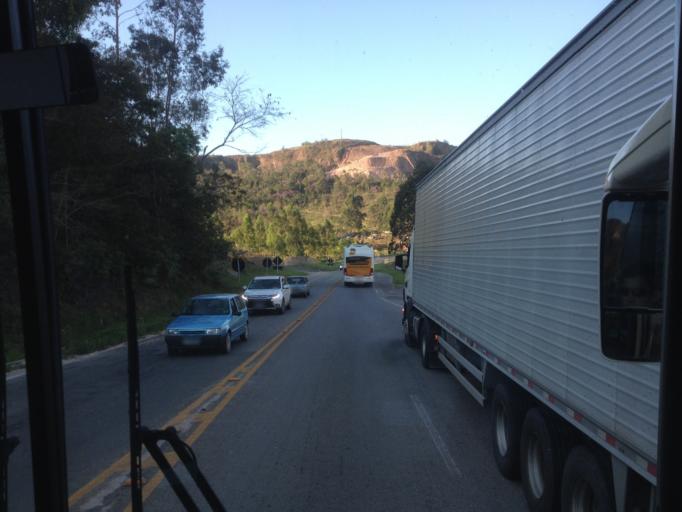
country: BR
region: Minas Gerais
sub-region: Juiz De Fora
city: Juiz de Fora
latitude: -21.6626
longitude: -43.3342
